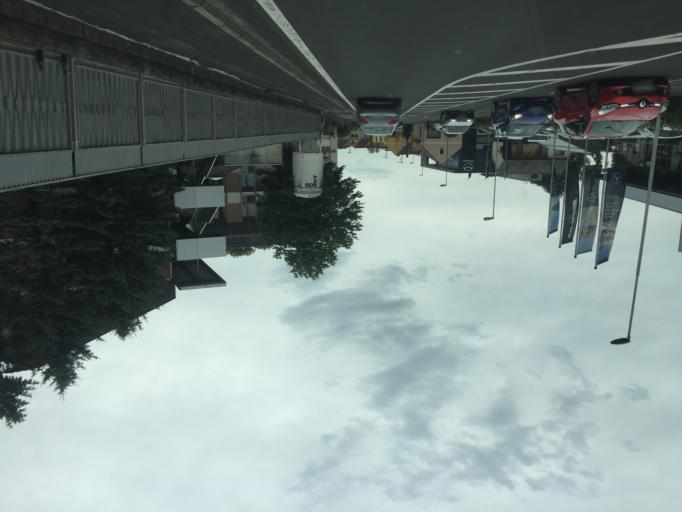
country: AT
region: Styria
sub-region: Politischer Bezirk Suedoststeiermark
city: Bad Radkersburg
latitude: 46.6912
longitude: 15.9850
